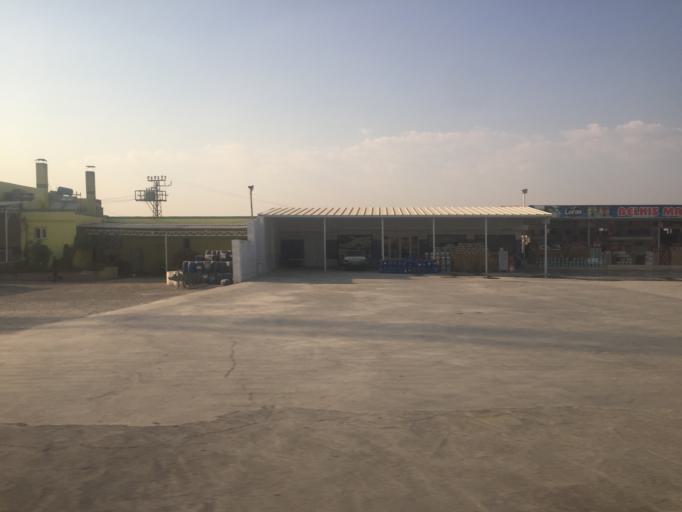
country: TR
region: Sanliurfa
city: Birecik
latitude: 37.0175
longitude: 37.8924
